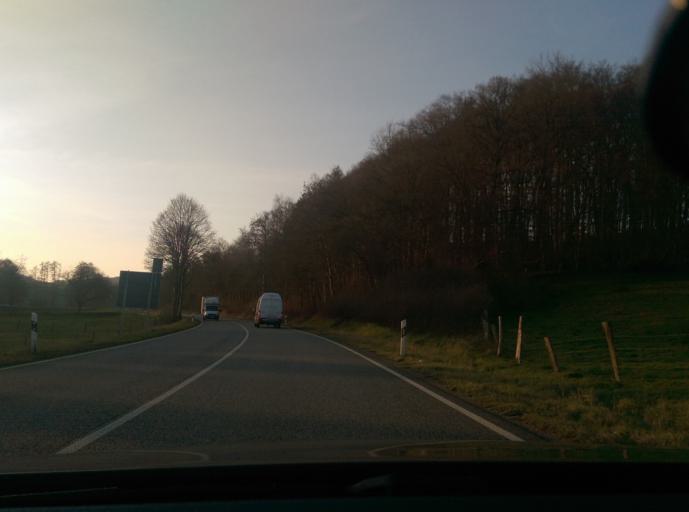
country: DE
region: Thuringia
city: Gerstungen
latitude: 51.0238
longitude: 10.0963
